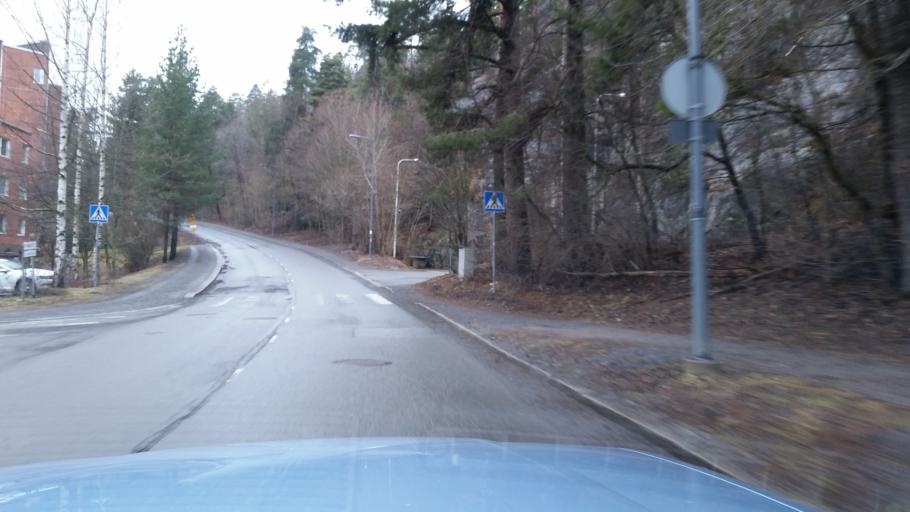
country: FI
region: Pirkanmaa
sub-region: Tampere
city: Tampere
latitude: 61.4941
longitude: 23.7233
